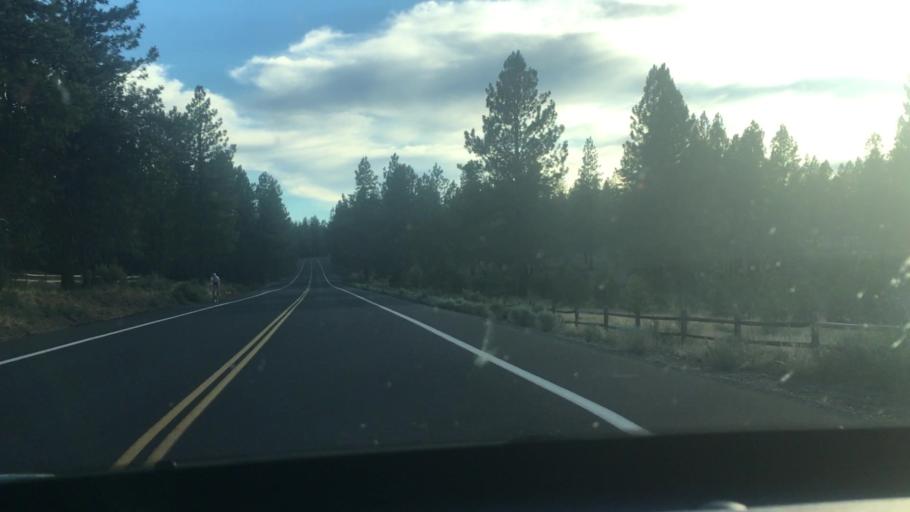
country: US
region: Oregon
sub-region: Deschutes County
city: Deschutes River Woods
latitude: 44.0514
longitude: -121.3792
